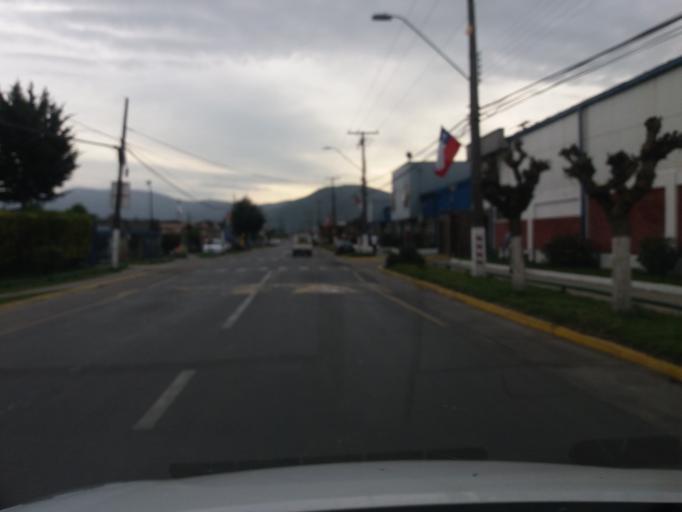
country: CL
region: Valparaiso
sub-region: Provincia de Quillota
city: Hacienda La Calera
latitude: -32.7786
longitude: -71.1873
